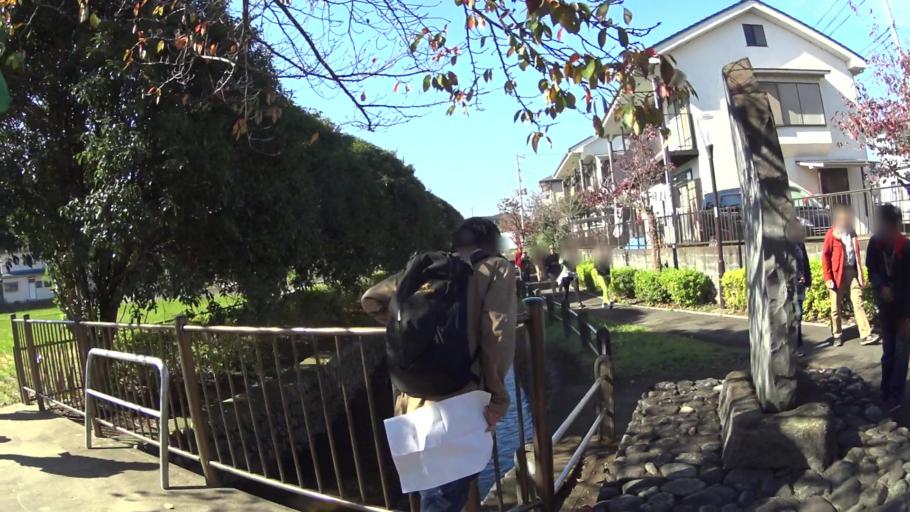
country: JP
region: Tokyo
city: Chofugaoka
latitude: 35.6480
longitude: 139.4981
